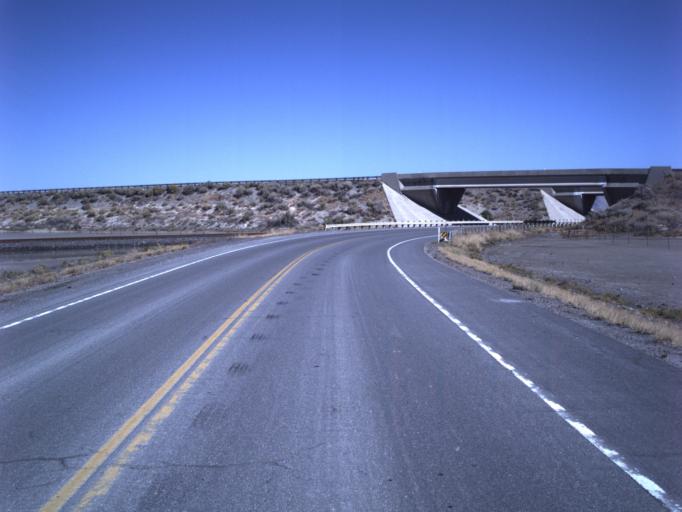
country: US
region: Utah
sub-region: Tooele County
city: Grantsville
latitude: 40.7078
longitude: -112.5302
